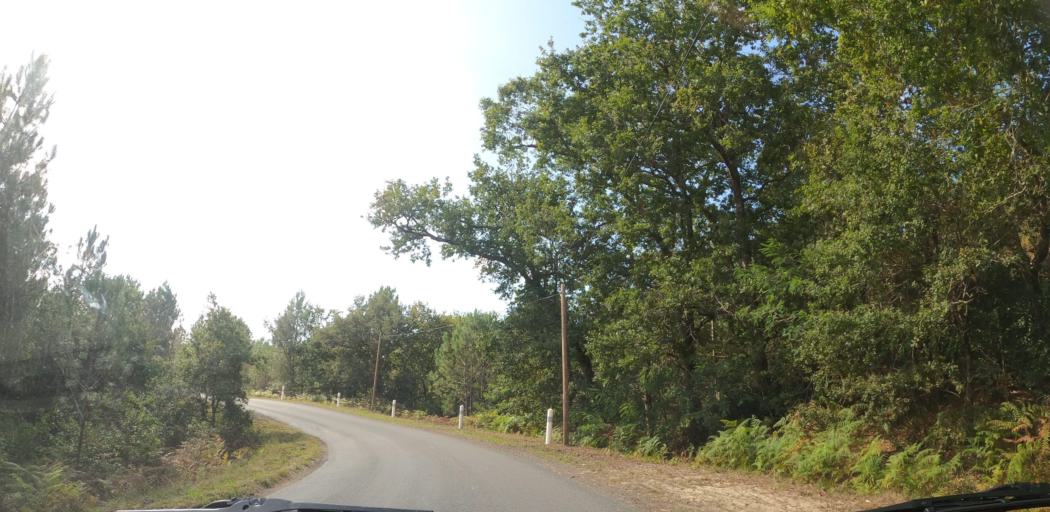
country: FR
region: Aquitaine
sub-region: Departement des Landes
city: Seignosse
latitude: 43.7131
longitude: -1.3757
